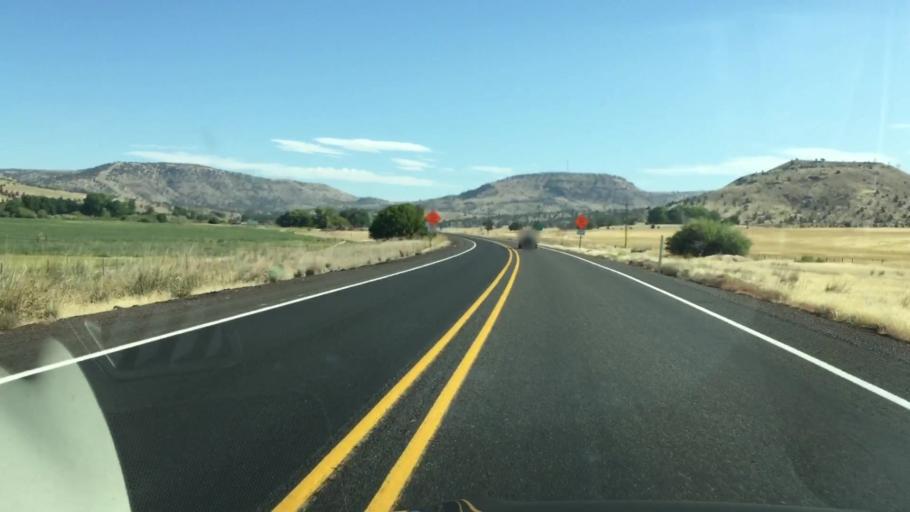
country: US
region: Oregon
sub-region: Jefferson County
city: Madras
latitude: 44.8019
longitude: -120.9375
